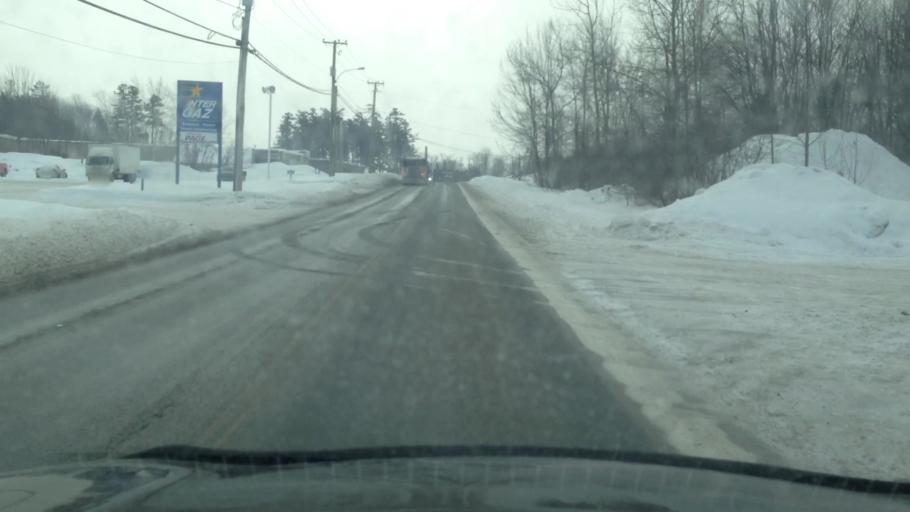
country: CA
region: Quebec
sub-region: Laurentides
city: Saint-Jerome
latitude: 45.7822
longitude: -74.0294
